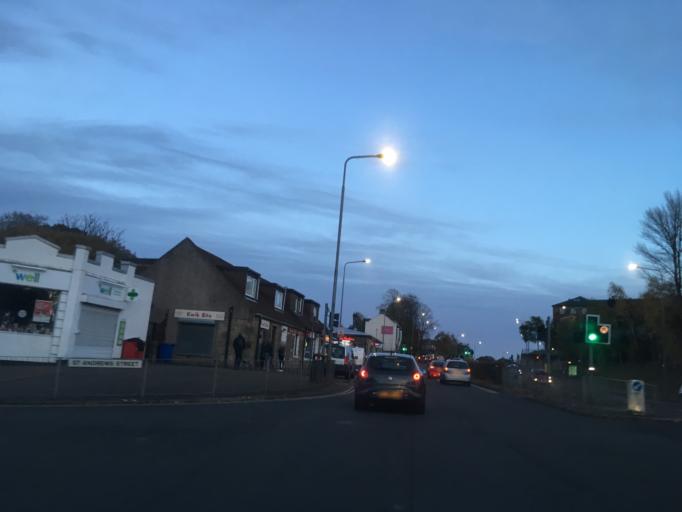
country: GB
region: Scotland
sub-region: Fife
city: Dunfermline
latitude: 56.0619
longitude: -3.4465
